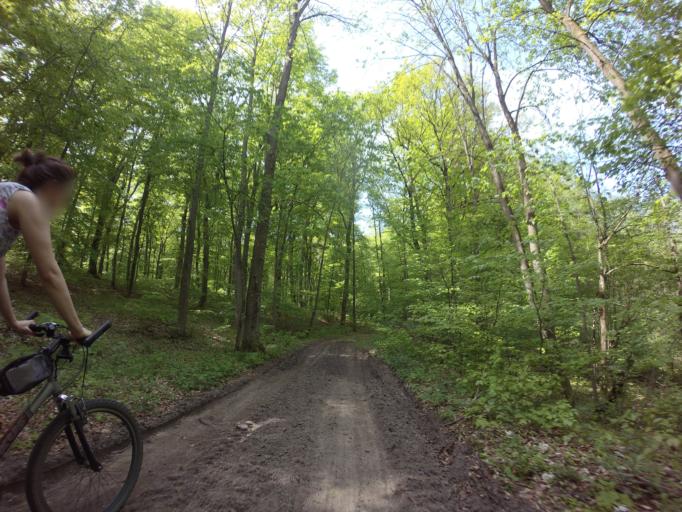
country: PL
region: West Pomeranian Voivodeship
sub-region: Powiat choszczenski
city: Choszczno
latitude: 53.2270
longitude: 15.4117
